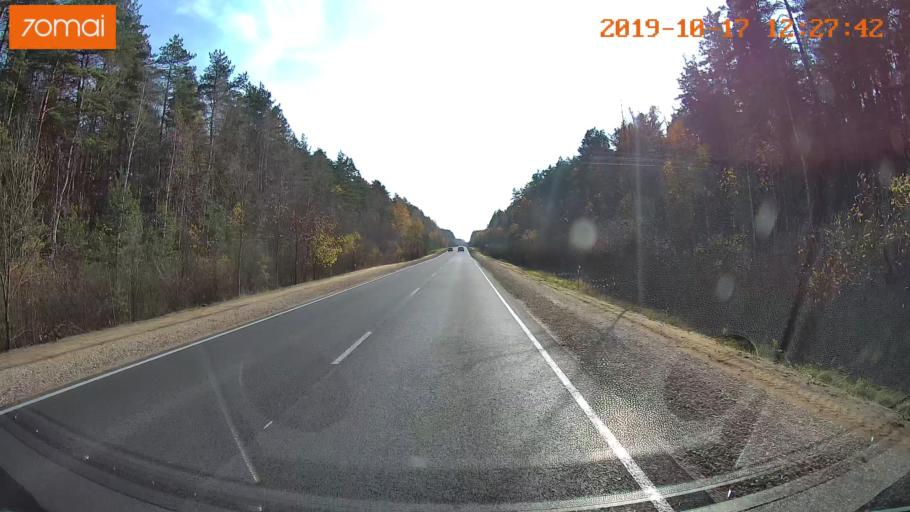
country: RU
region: Rjazan
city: Syntul
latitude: 54.9999
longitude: 41.2645
